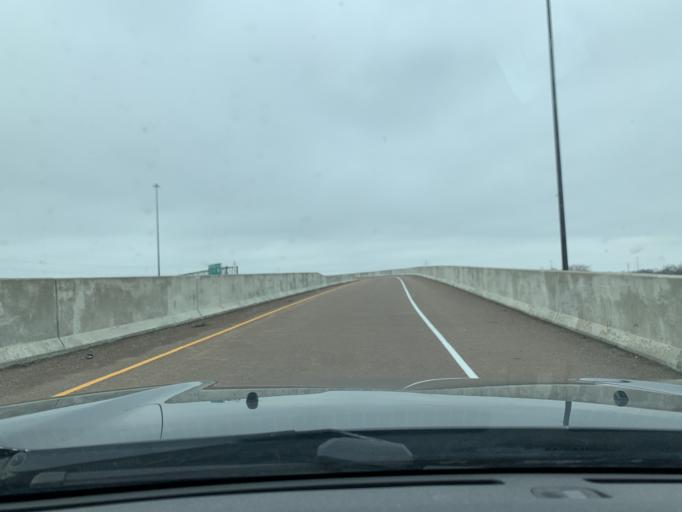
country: US
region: Indiana
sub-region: Lake County
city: Highland
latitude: 41.5746
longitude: -87.4599
